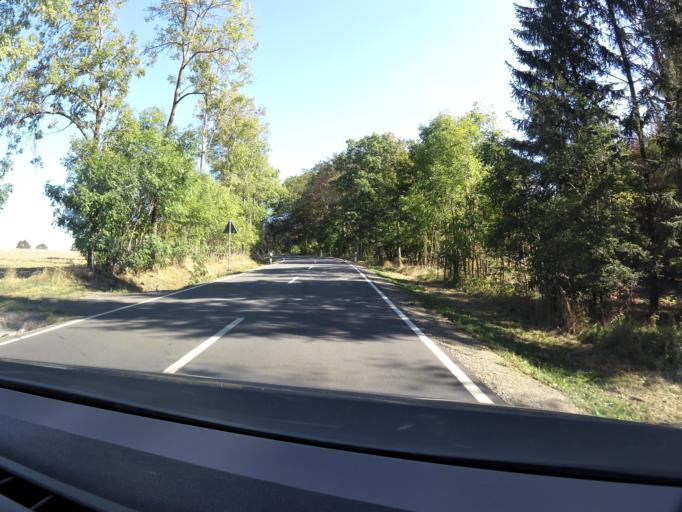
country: DE
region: Saxony-Anhalt
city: Hasselfelde
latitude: 51.6725
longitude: 10.8955
